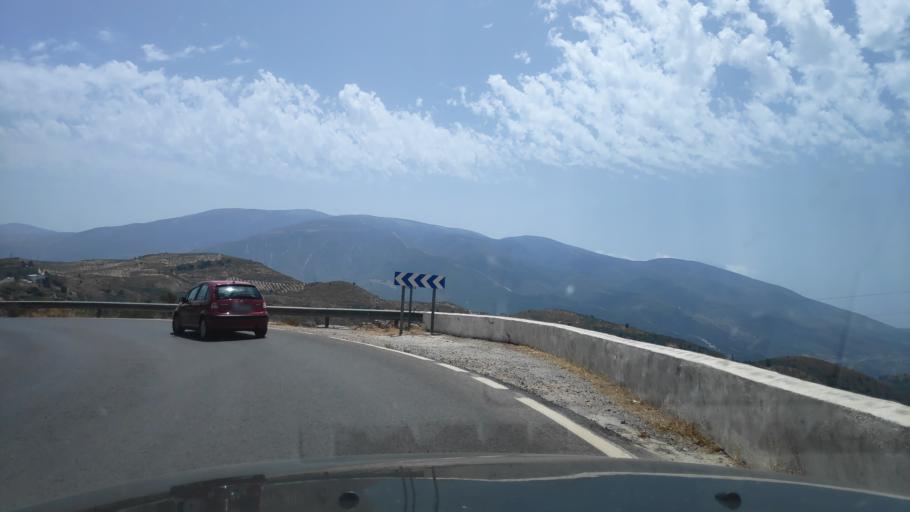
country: ES
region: Andalusia
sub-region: Provincia de Granada
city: Lanjaron
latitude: 36.9116
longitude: -3.4761
